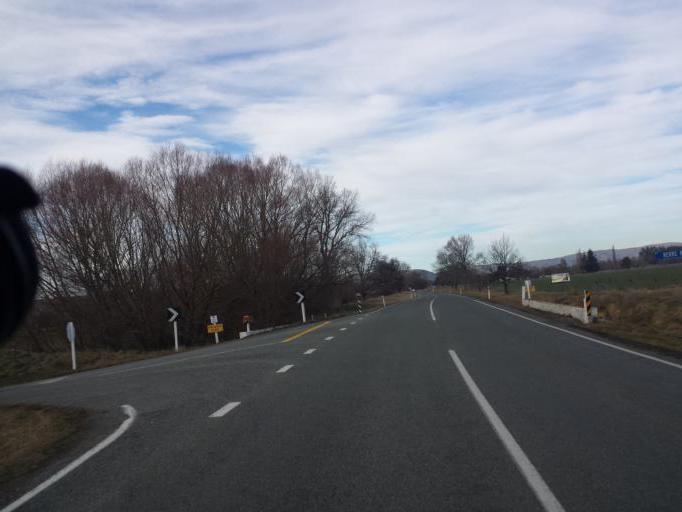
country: NZ
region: Canterbury
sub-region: Timaru District
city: Pleasant Point
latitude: -44.0824
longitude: 170.8092
